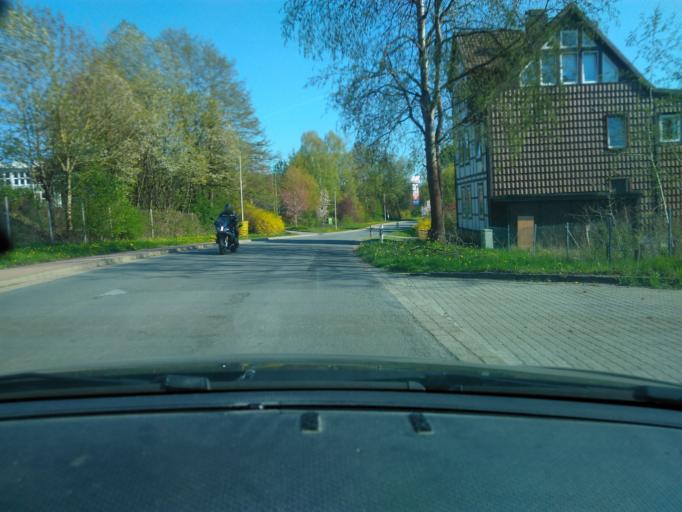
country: DE
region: Lower Saxony
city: Osterode am Harz
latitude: 51.7192
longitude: 10.2709
